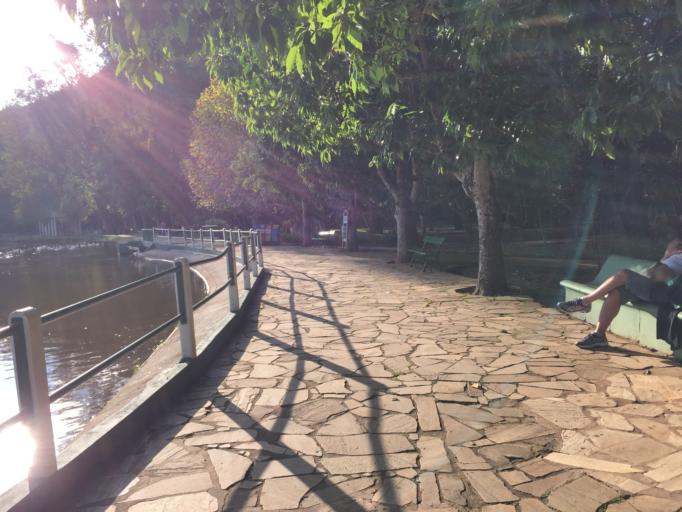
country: BR
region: Minas Gerais
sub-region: Caxambu
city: Caxambu
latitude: -21.9839
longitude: -44.9371
